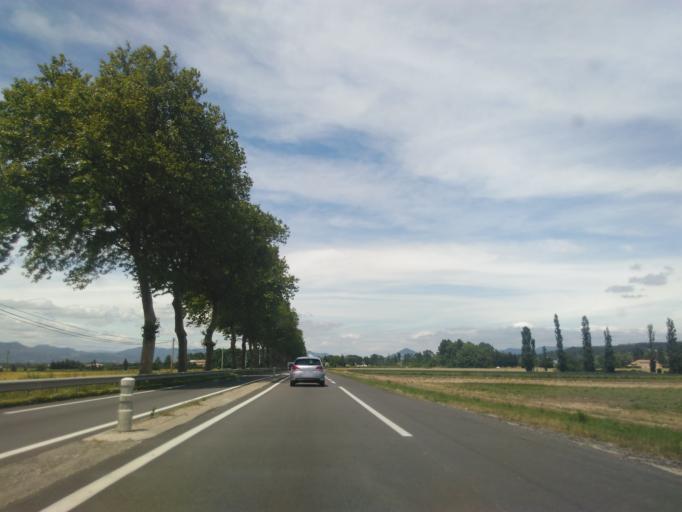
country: FR
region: Rhone-Alpes
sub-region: Departement de la Drome
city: Malataverne
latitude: 44.4995
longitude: 4.7435
